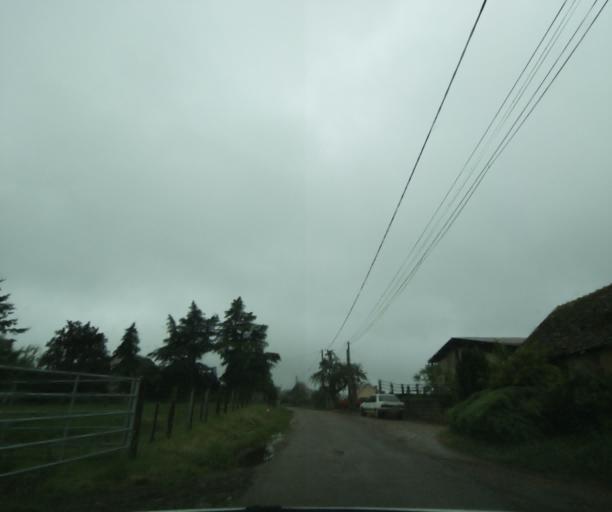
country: FR
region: Bourgogne
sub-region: Departement de Saone-et-Loire
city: Charolles
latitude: 46.4570
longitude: 4.2105
